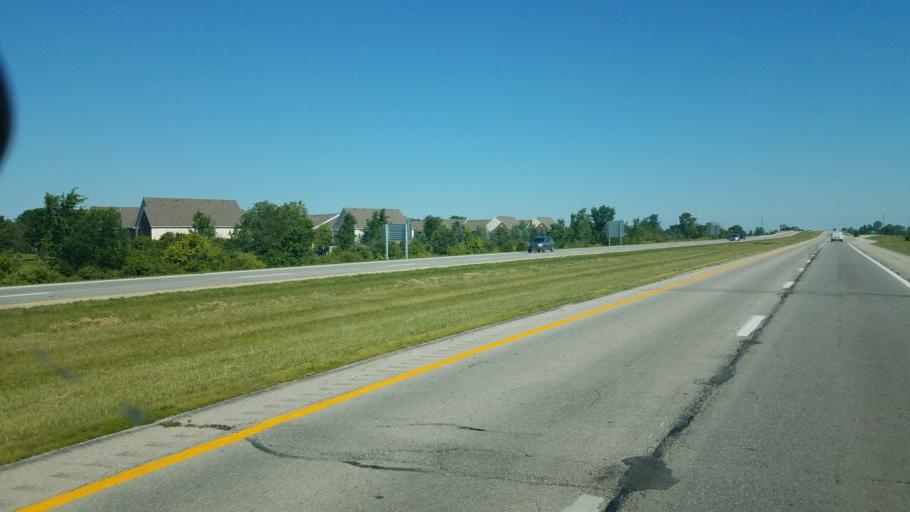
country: US
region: Ohio
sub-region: Marion County
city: Marion
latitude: 40.5892
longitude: -83.0804
